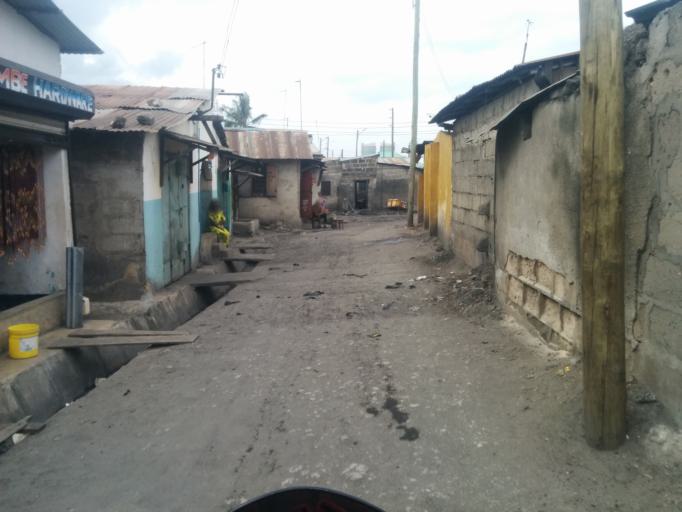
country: TZ
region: Dar es Salaam
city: Dar es Salaam
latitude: -6.8354
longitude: 39.2771
